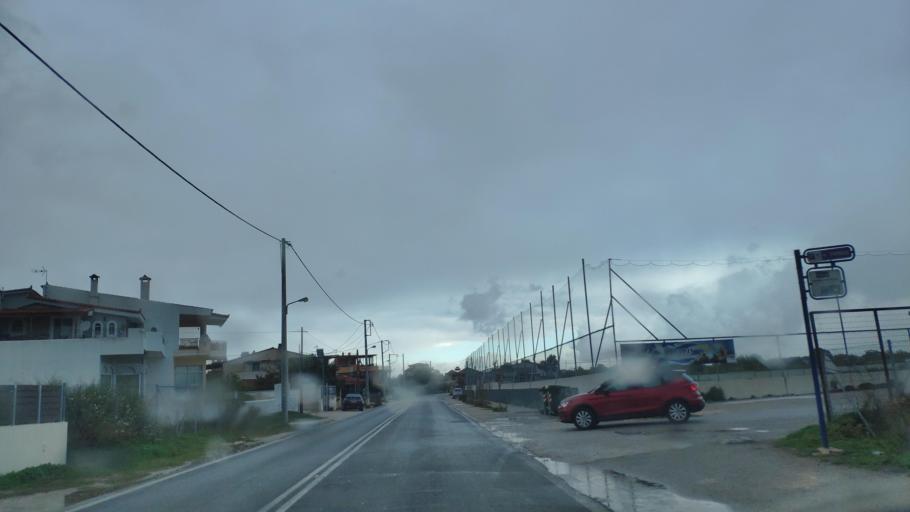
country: GR
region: Attica
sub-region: Nomarchia Anatolikis Attikis
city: Artemida
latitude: 37.9865
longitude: 24.0129
